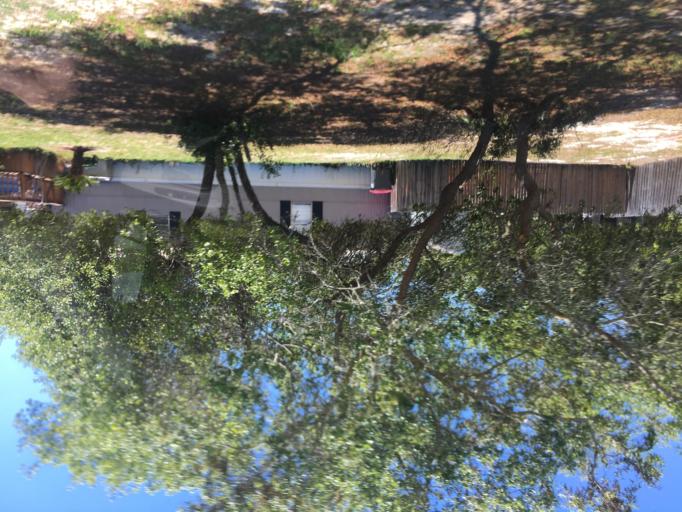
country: US
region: Florida
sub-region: Bay County
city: Laguna Beach
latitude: 30.2643
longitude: -85.9622
